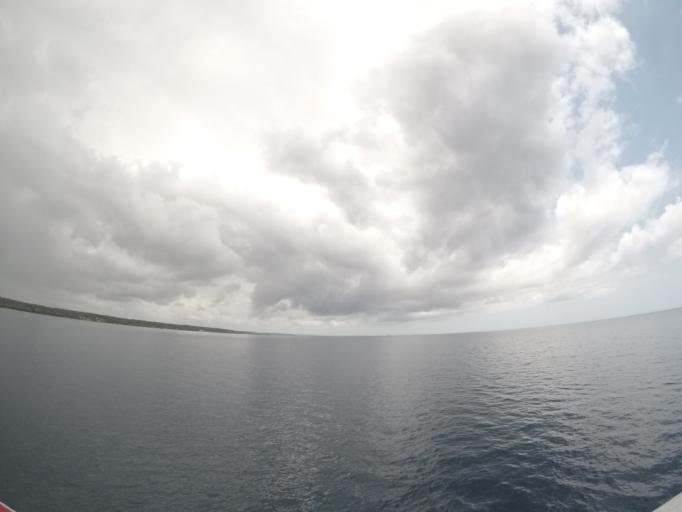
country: TZ
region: Zanzibar North
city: Mkokotoni
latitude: -5.9729
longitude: 39.1708
